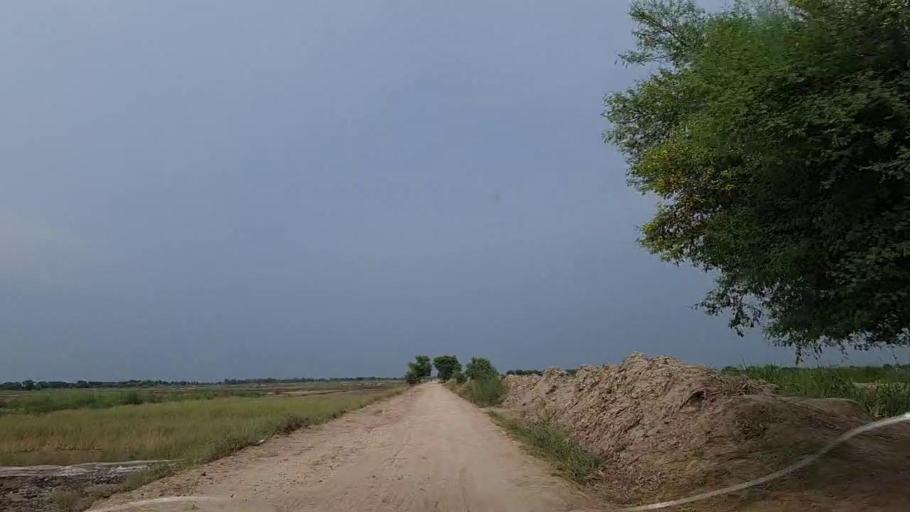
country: PK
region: Sindh
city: Khanpur
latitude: 27.8352
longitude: 69.5805
